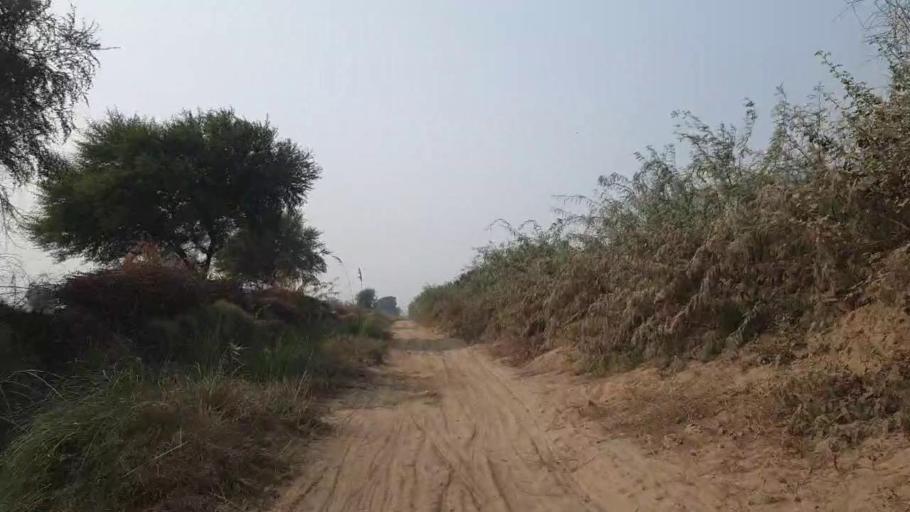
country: PK
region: Sindh
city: Tando Muhammad Khan
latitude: 25.1907
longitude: 68.5866
